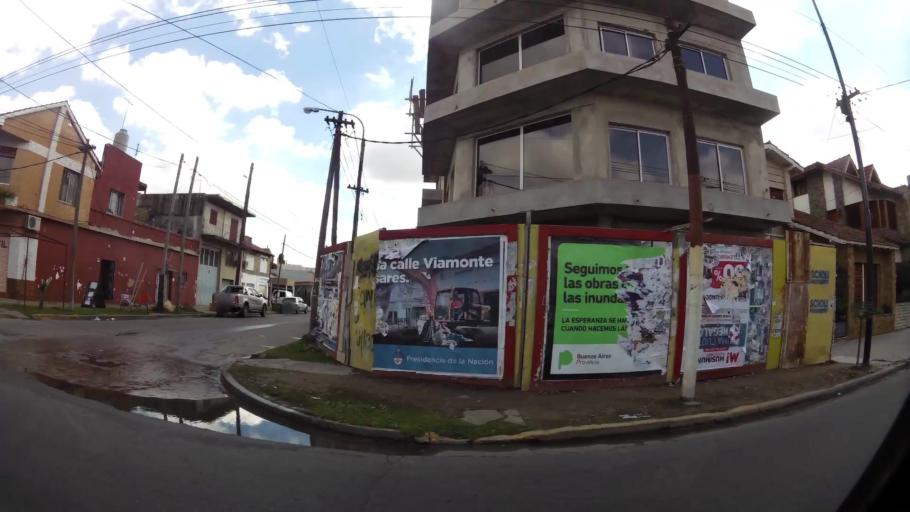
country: AR
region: Buenos Aires
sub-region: Partido de Lanus
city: Lanus
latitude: -34.6892
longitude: -58.4106
